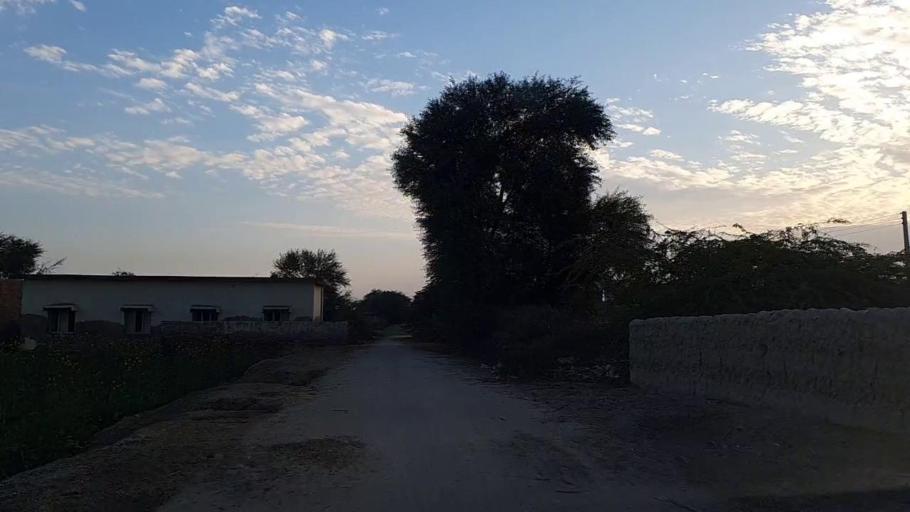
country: PK
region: Sindh
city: Daur
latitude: 26.4131
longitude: 68.4774
